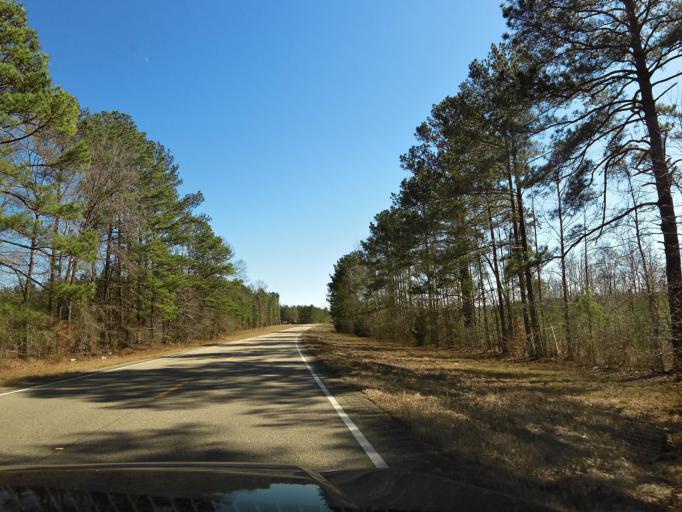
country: US
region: Alabama
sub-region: Montgomery County
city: Pike Road
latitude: 32.1673
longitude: -86.0639
